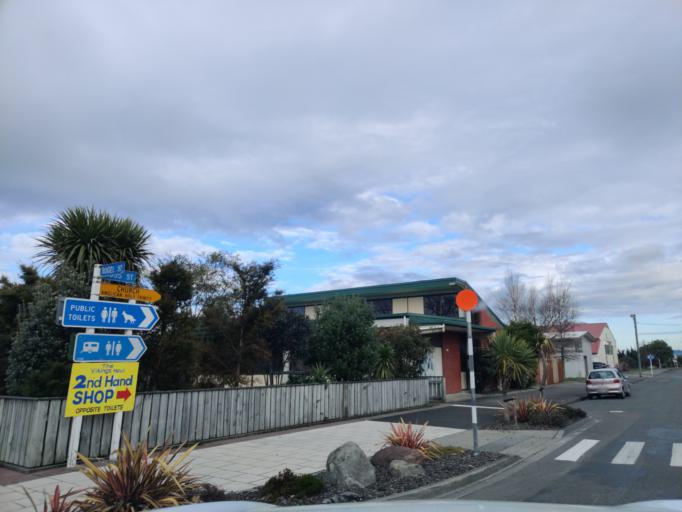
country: NZ
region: Manawatu-Wanganui
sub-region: Palmerston North City
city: Palmerston North
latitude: -40.3379
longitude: 175.8694
